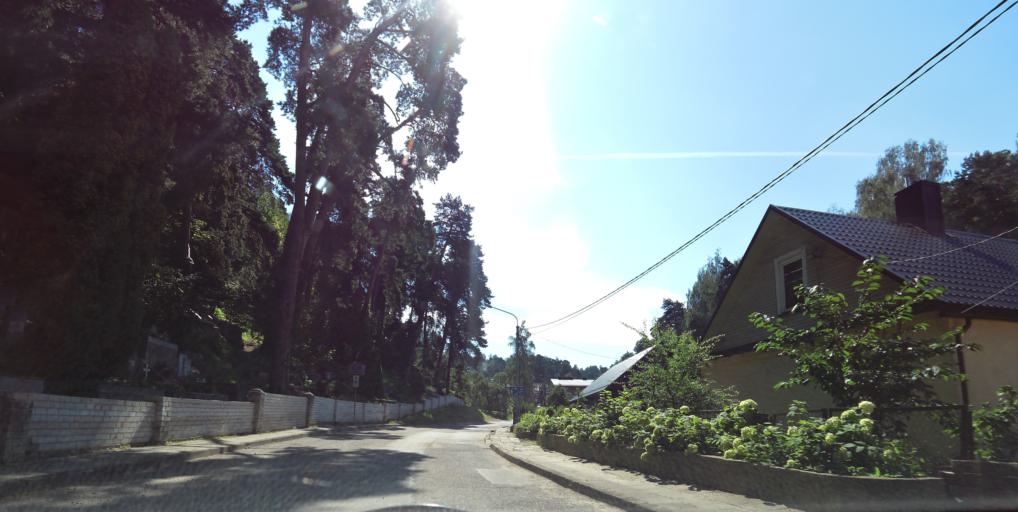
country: LT
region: Vilnius County
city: Rasos
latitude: 54.6943
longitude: 25.3110
